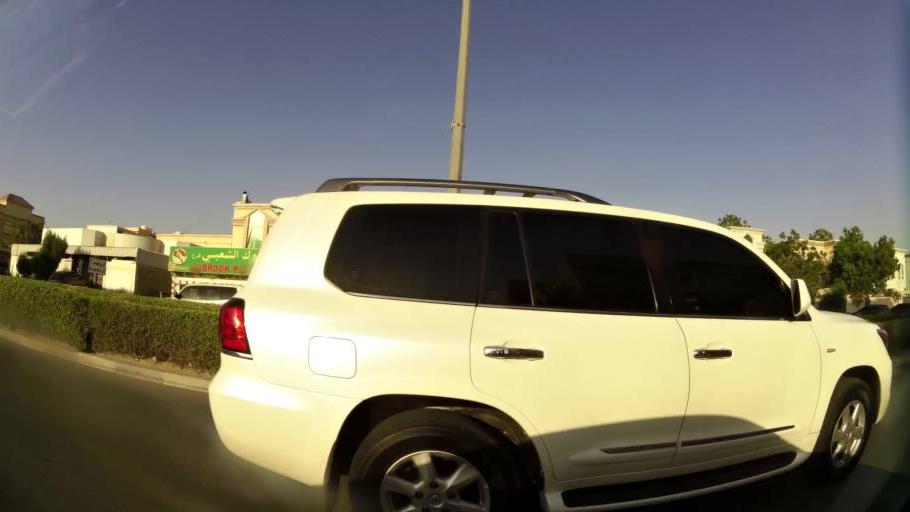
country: AE
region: Ajman
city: Ajman
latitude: 25.3922
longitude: 55.5055
